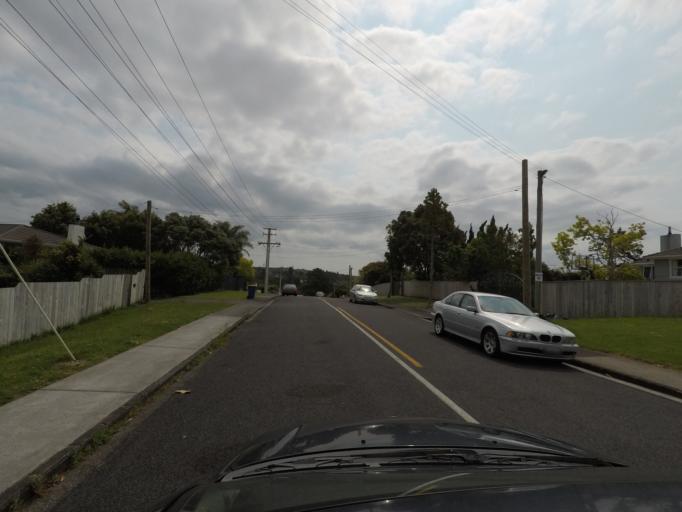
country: NZ
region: Auckland
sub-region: Auckland
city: Rosebank
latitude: -36.8317
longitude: 174.6456
